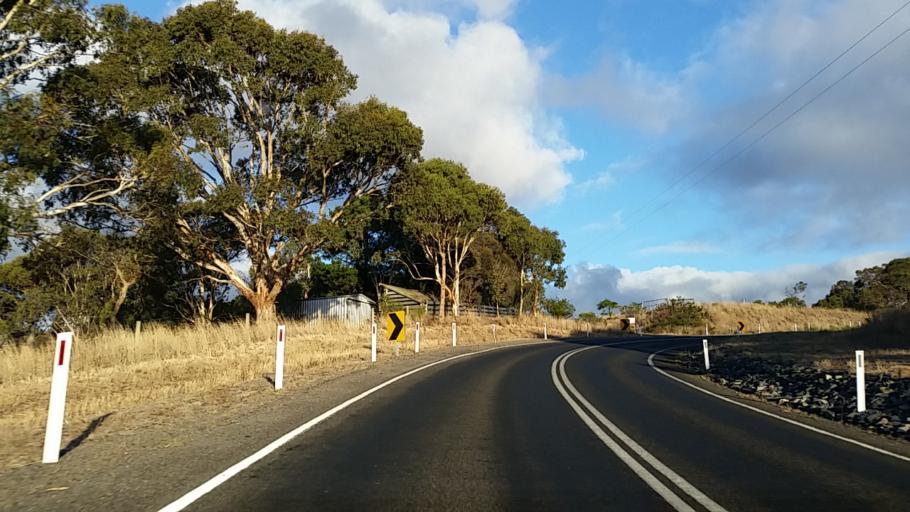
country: AU
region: South Australia
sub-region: Yankalilla
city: Normanville
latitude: -35.5543
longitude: 138.1989
